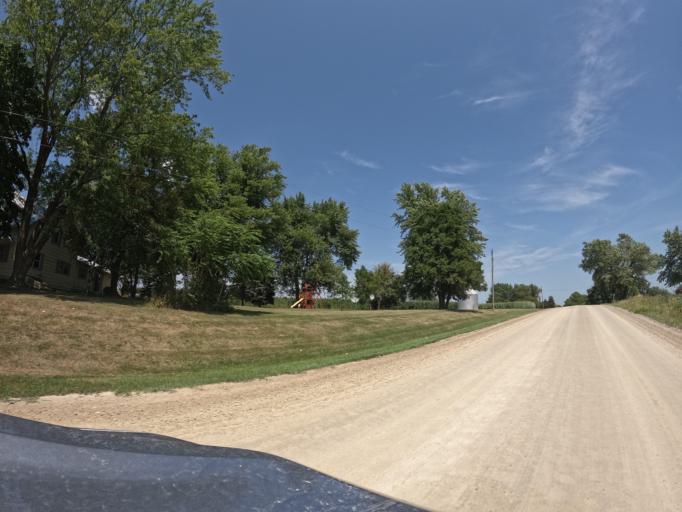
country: US
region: Iowa
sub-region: Henry County
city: Mount Pleasant
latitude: 40.9482
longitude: -91.6043
